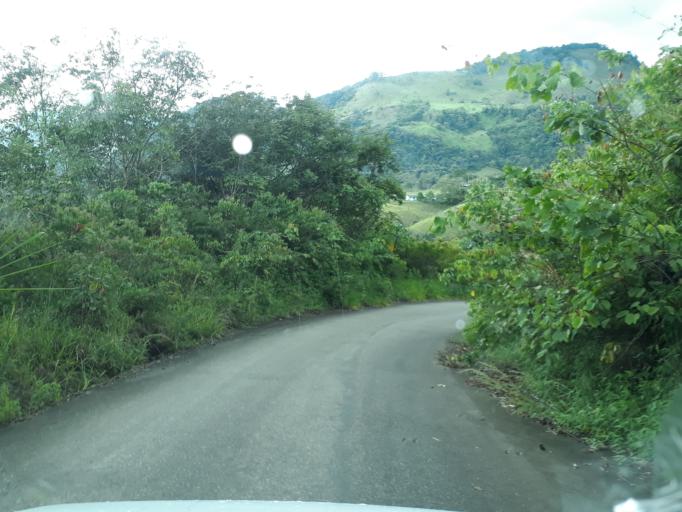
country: CO
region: Cundinamarca
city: Medina
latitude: 4.5840
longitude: -73.3682
